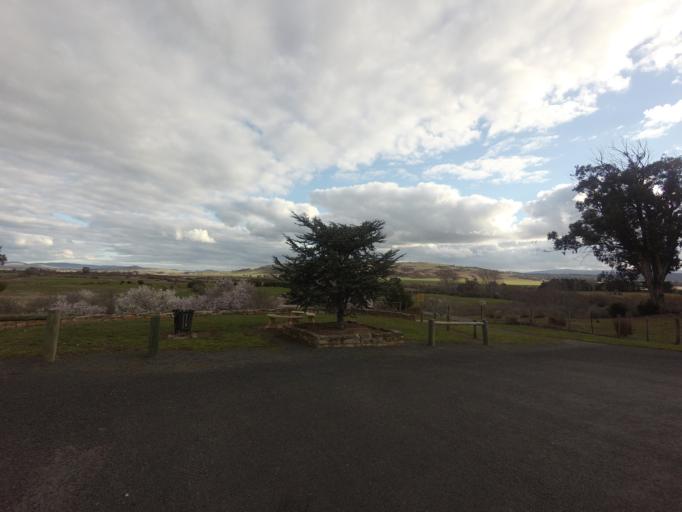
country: AU
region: Tasmania
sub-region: Northern Midlands
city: Evandale
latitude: -42.0326
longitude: 147.4918
